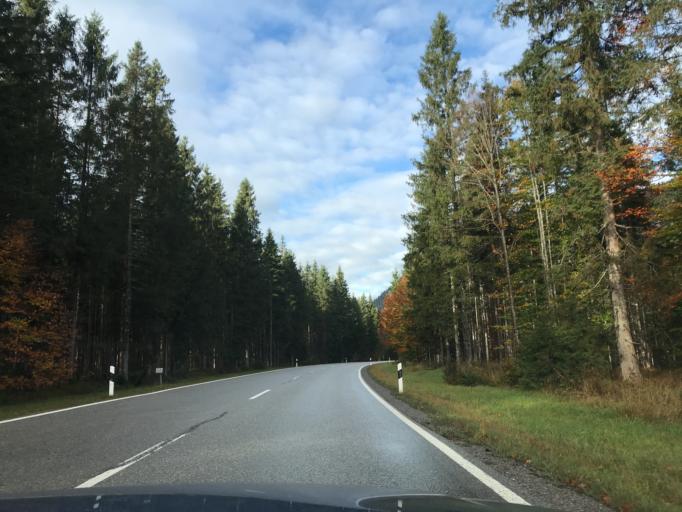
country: DE
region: Bavaria
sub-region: Upper Bavaria
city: Jachenau
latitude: 47.5566
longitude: 11.4492
